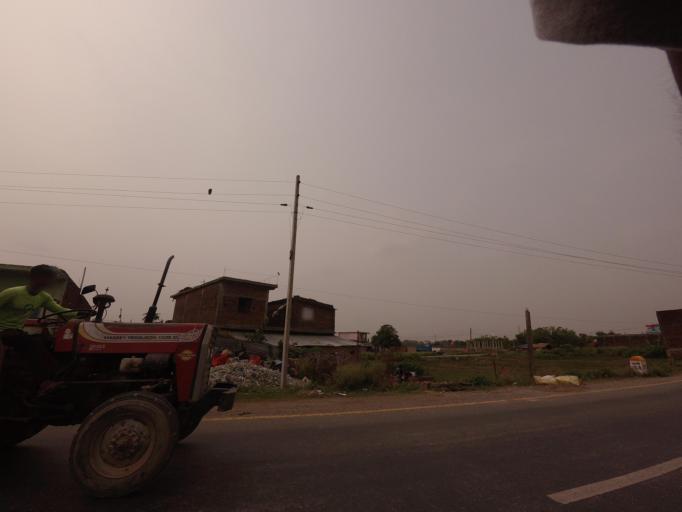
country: IN
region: Uttar Pradesh
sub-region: Maharajganj
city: Nautanwa
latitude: 27.5021
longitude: 83.3415
